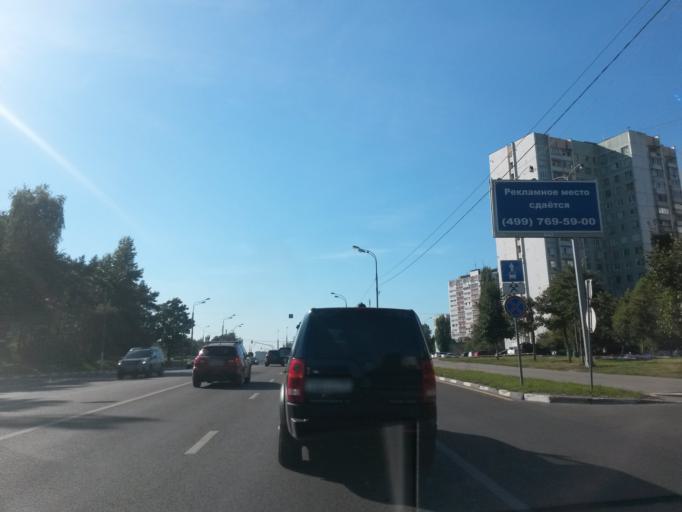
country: RU
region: Moscow
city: Zyuzino
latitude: 55.6488
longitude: 37.5675
